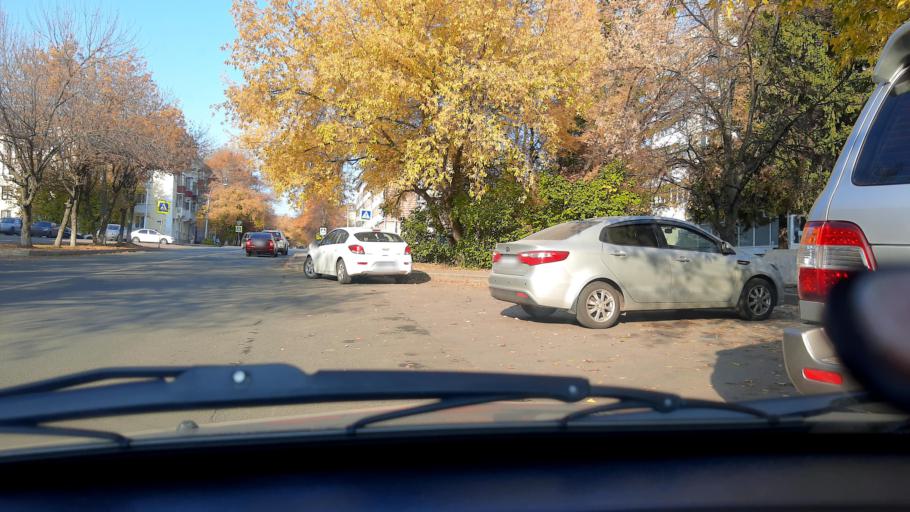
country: RU
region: Bashkortostan
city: Ufa
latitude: 54.8154
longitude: 56.0668
